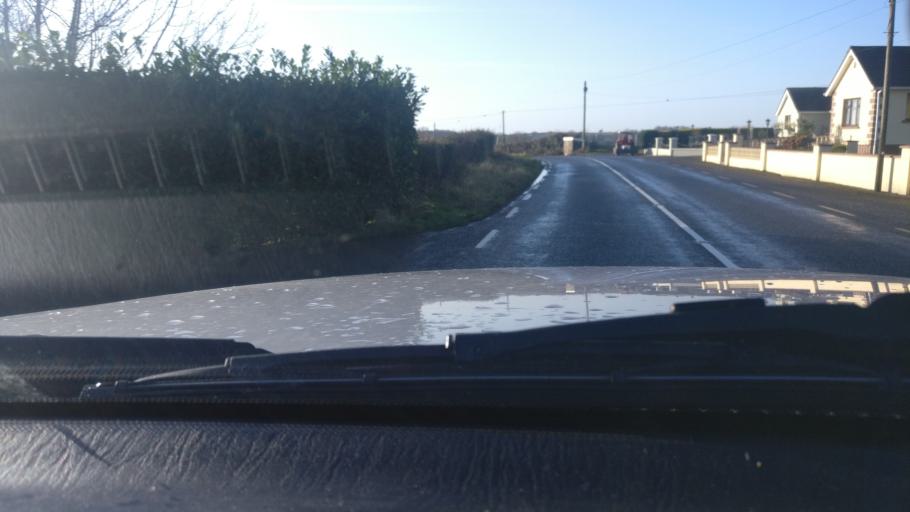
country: IE
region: Leinster
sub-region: An Longfort
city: Granard
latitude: 53.8143
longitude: -7.3695
